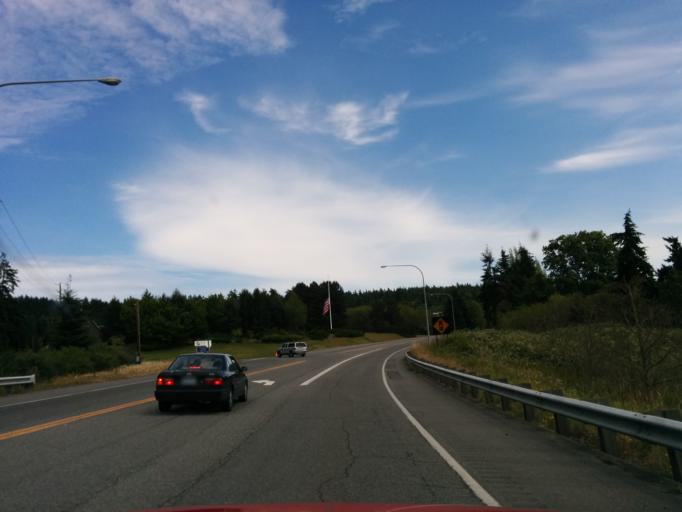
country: US
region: Washington
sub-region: Island County
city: Freeland
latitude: 48.0076
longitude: -122.4662
